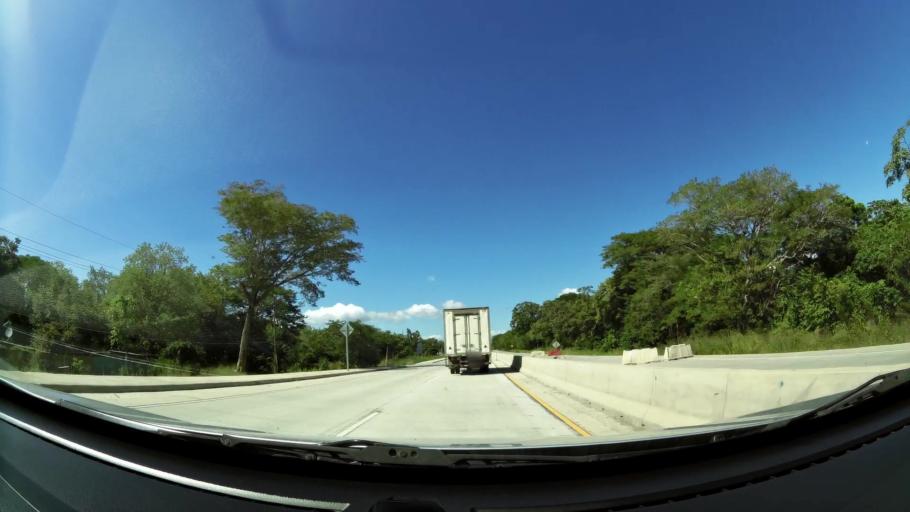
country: CR
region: Guanacaste
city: Liberia
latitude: 10.5902
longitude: -85.4200
